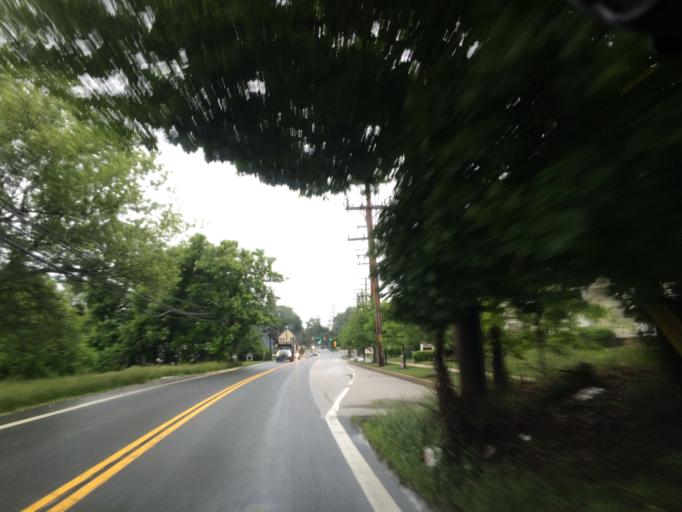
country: US
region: Maryland
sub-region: Howard County
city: Highland
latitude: 39.1808
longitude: -76.9562
